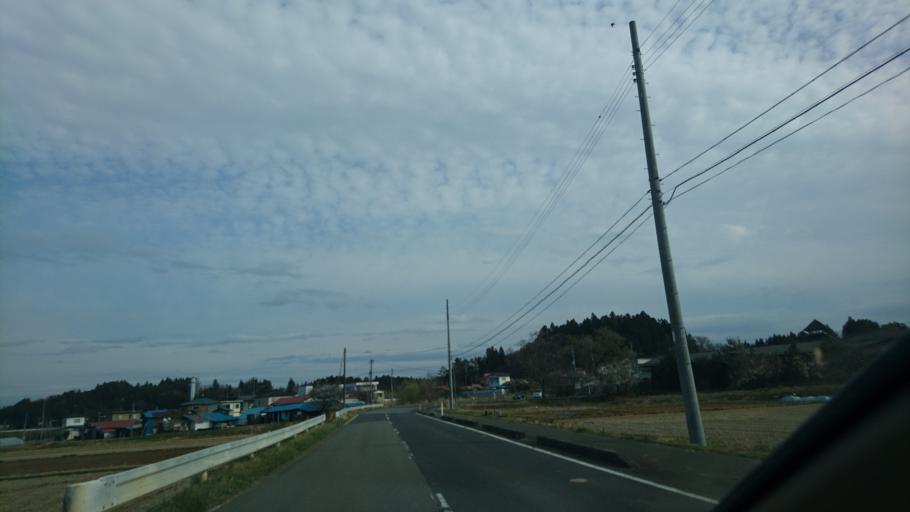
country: JP
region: Iwate
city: Ichinoseki
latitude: 38.7982
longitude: 141.0503
